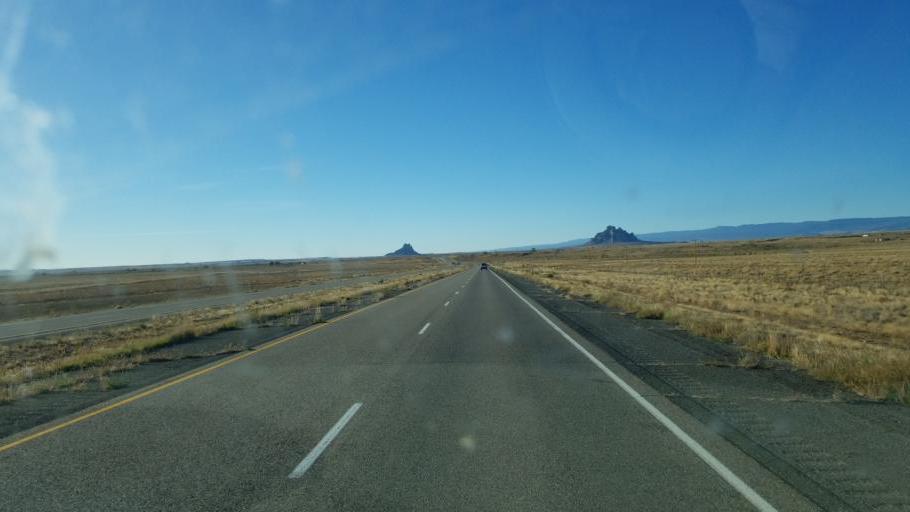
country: US
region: New Mexico
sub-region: San Juan County
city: Shiprock
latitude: 36.4696
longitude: -108.7244
